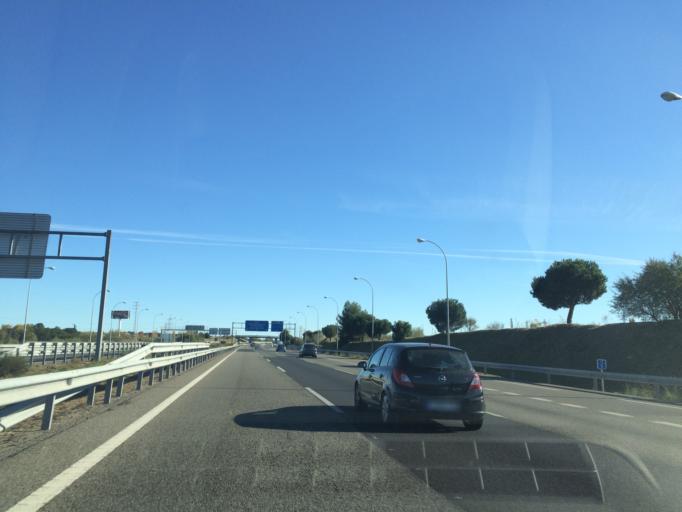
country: ES
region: Madrid
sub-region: Provincia de Madrid
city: Pozuelo de Alarcon
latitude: 40.4187
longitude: -3.8271
